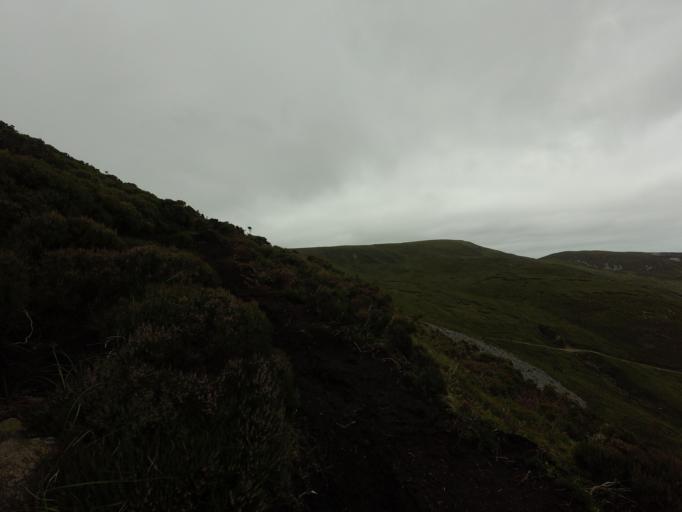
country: IE
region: Ulster
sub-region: County Donegal
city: Killybegs
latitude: 54.6423
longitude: -8.6844
